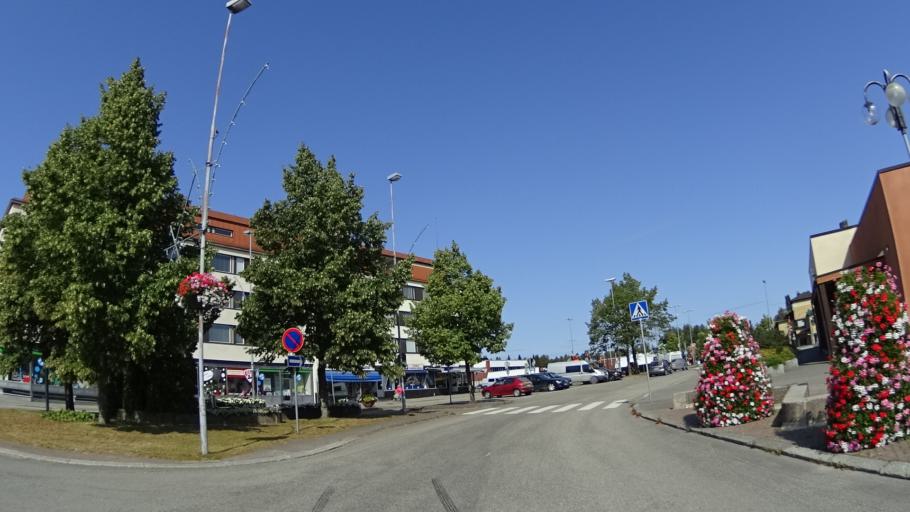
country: FI
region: Pirkanmaa
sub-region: Ylae-Pirkanmaa
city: Maenttae
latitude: 62.0293
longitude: 24.6236
